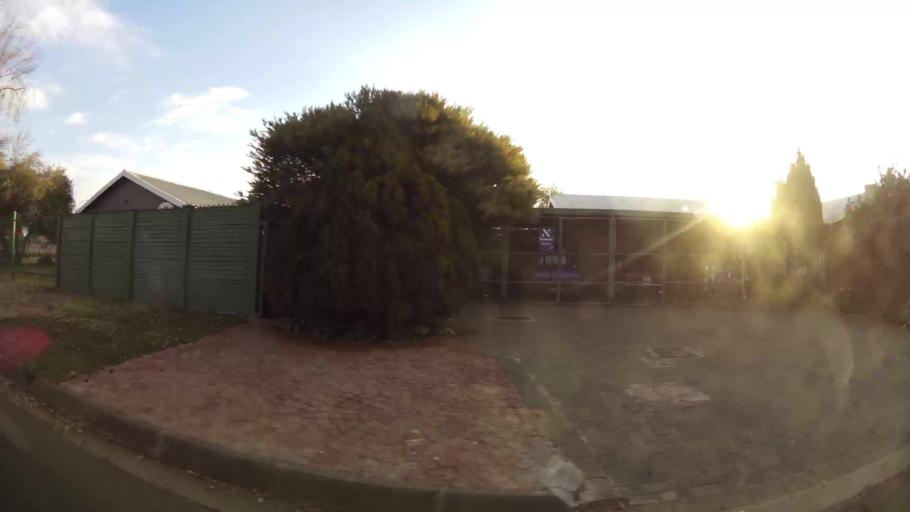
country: ZA
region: Orange Free State
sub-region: Mangaung Metropolitan Municipality
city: Bloemfontein
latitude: -29.1388
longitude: 26.1878
